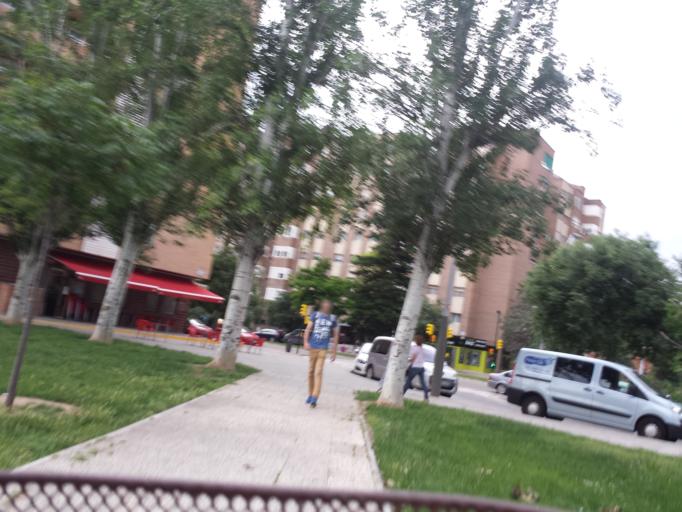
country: ES
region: Aragon
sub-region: Provincia de Zaragoza
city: Almozara
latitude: 41.6623
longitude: -0.9038
